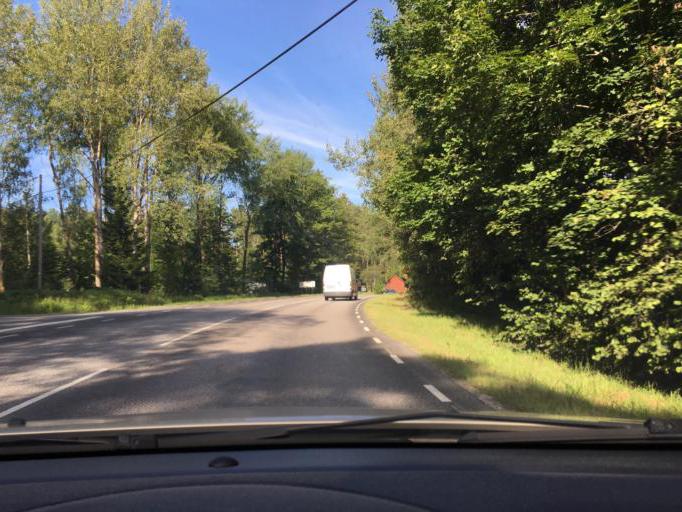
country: SE
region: Stockholm
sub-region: Sodertalje Kommun
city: Soedertaelje
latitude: 59.2158
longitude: 17.6635
